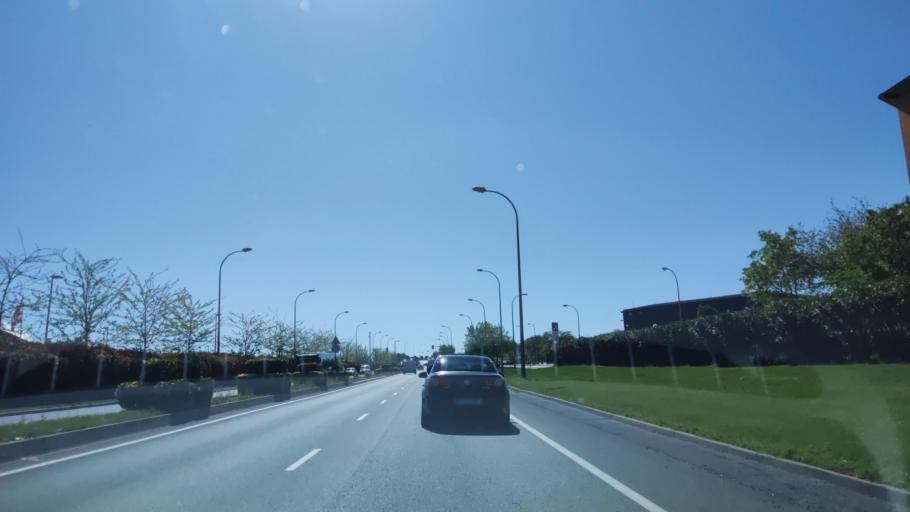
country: ES
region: Madrid
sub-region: Provincia de Madrid
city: San Blas
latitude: 40.4346
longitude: -3.6056
